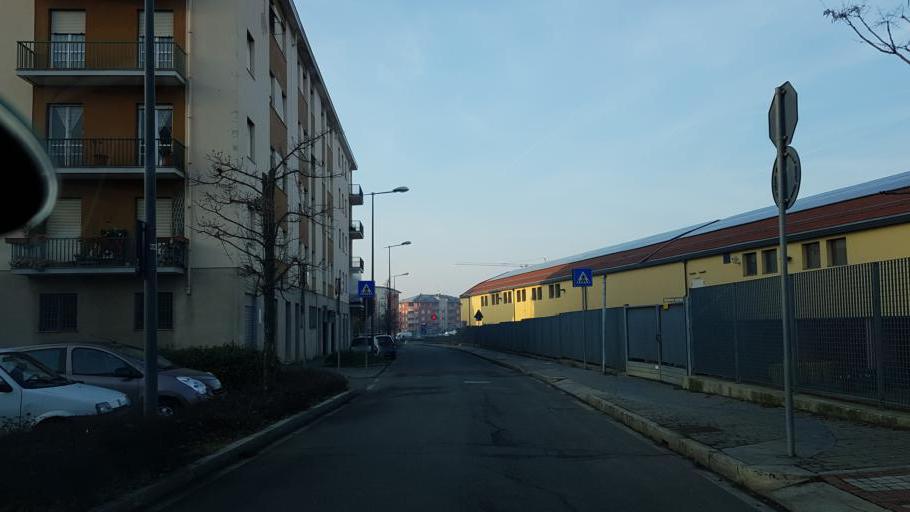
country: IT
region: Piedmont
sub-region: Provincia di Alessandria
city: Novi Ligure
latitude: 44.7629
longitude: 8.7791
